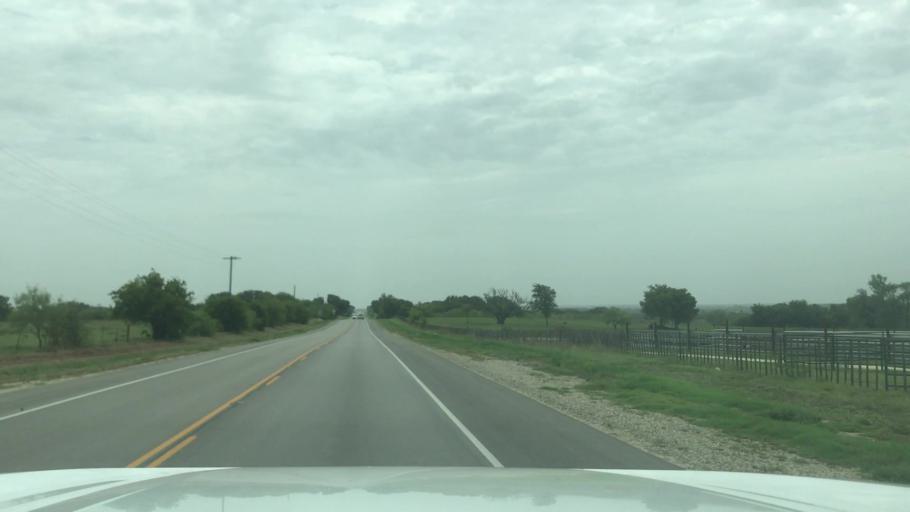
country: US
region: Texas
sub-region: Erath County
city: Dublin
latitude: 32.0860
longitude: -98.2547
